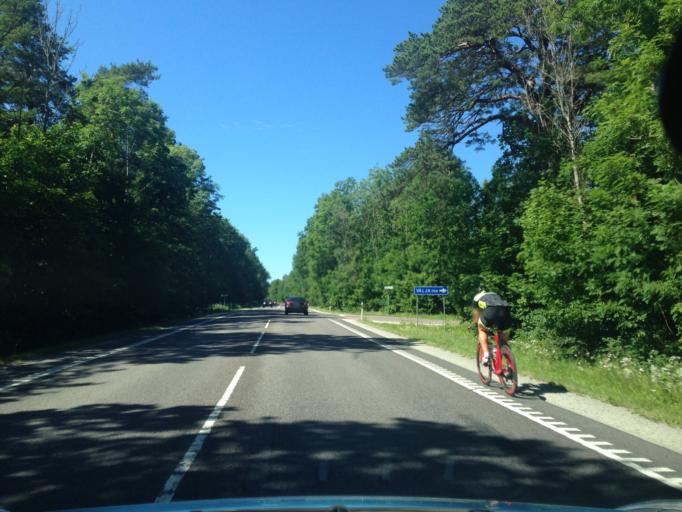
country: EE
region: Harju
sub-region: Saue linn
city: Saue
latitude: 59.3171
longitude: 24.5079
